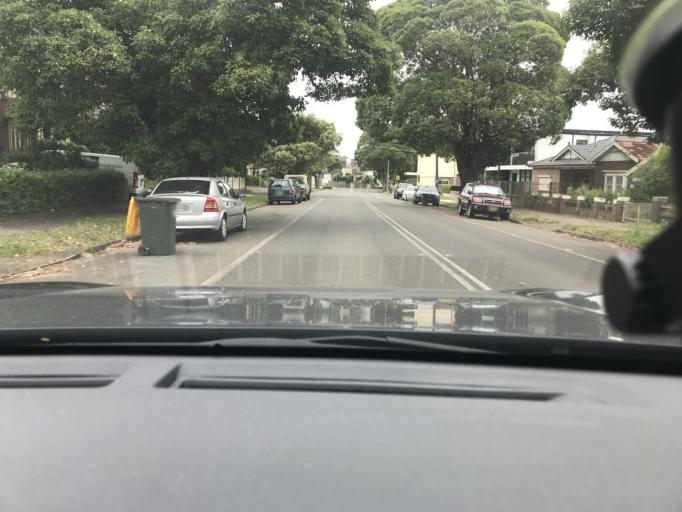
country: AU
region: New South Wales
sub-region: Canada Bay
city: Concord
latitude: -33.8605
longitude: 151.1103
